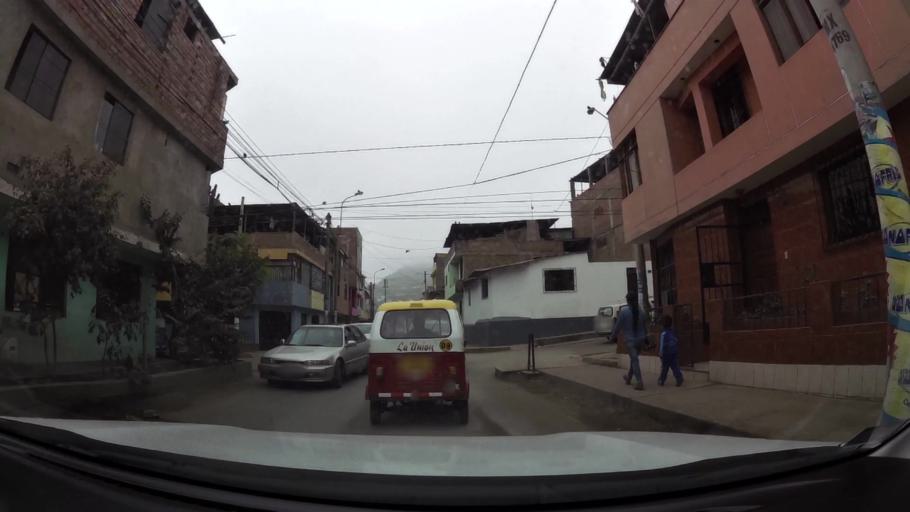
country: PE
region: Lima
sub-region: Lima
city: Surco
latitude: -12.1572
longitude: -76.9529
